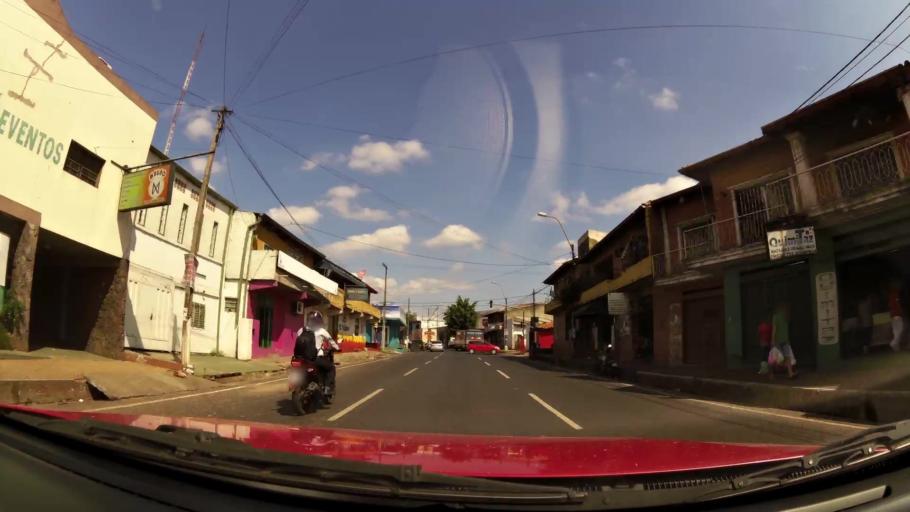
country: PY
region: Central
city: Fernando de la Mora
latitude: -25.3443
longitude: -57.5168
